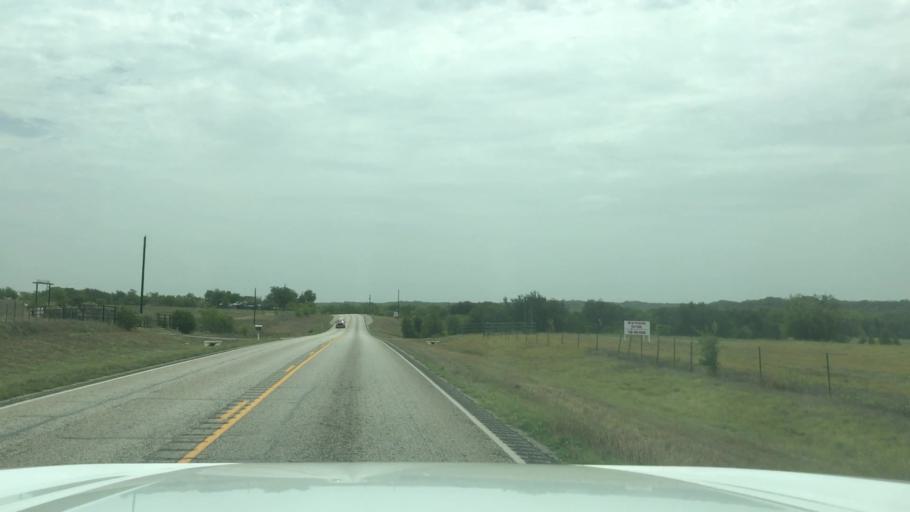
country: US
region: Texas
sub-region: Hamilton County
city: Hico
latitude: 32.0439
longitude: -98.1390
